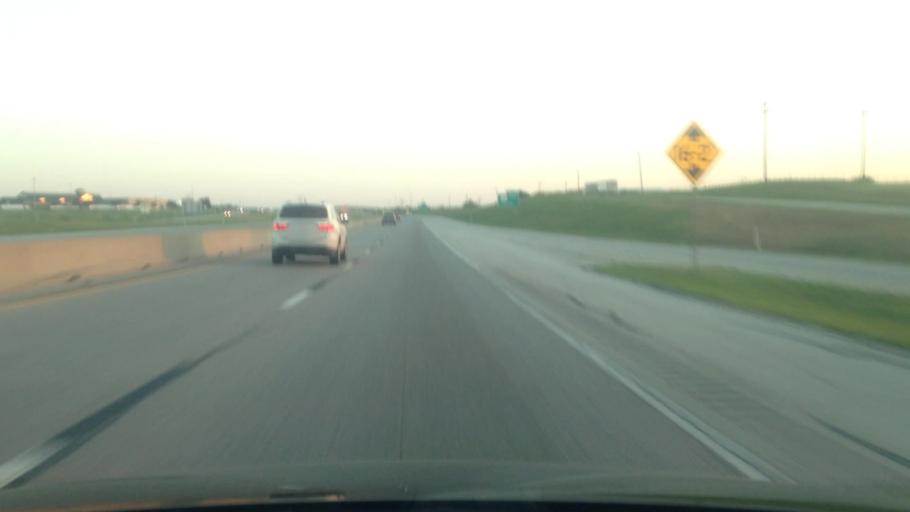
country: US
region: Texas
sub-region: Tarrant County
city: Haslet
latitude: 32.9696
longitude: -97.3098
